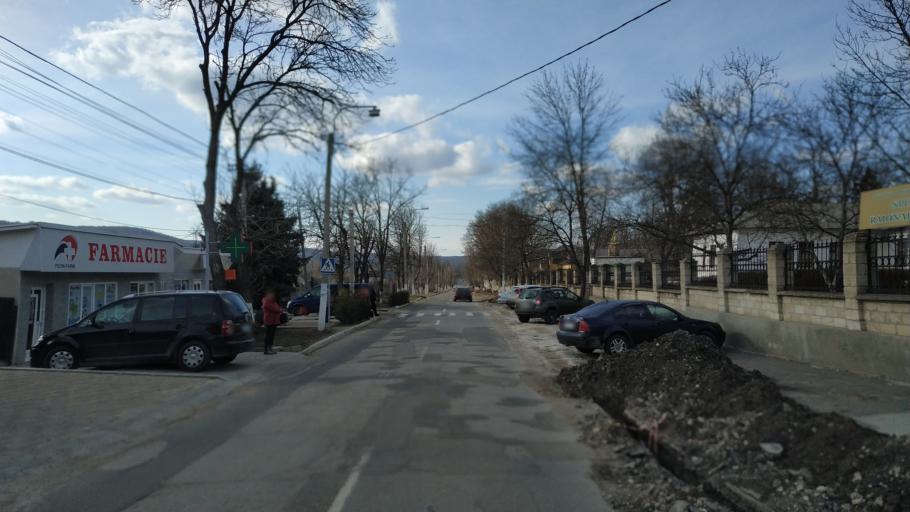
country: MD
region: Hincesti
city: Hincesti
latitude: 46.8330
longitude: 28.5825
